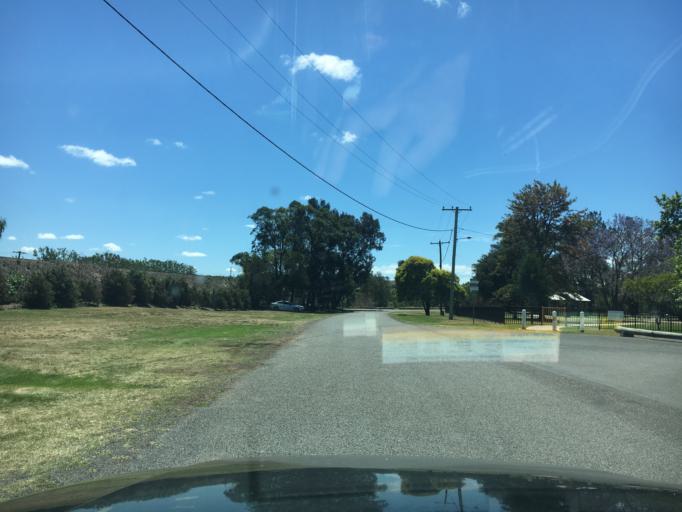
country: AU
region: New South Wales
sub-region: Singleton
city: Singleton
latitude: -32.5657
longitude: 151.1595
